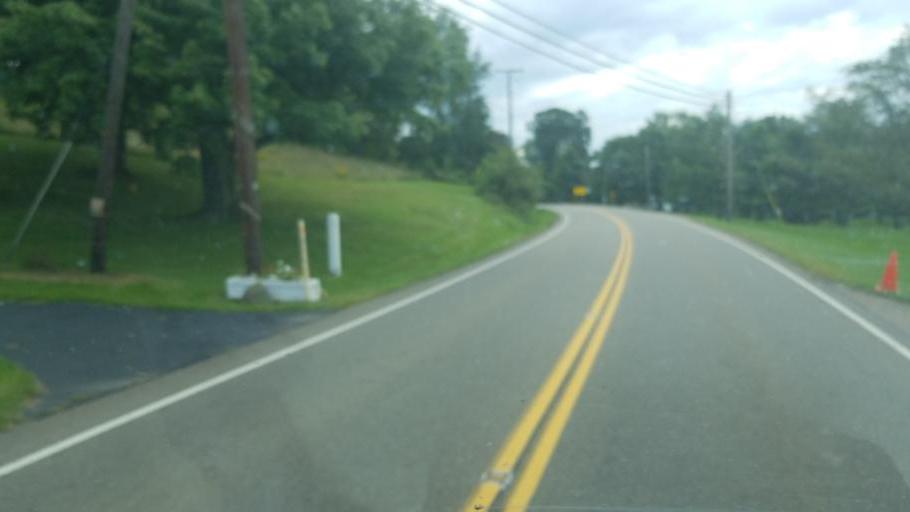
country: US
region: Ohio
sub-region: Carroll County
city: Lake Mohawk
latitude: 40.6614
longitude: -81.2866
